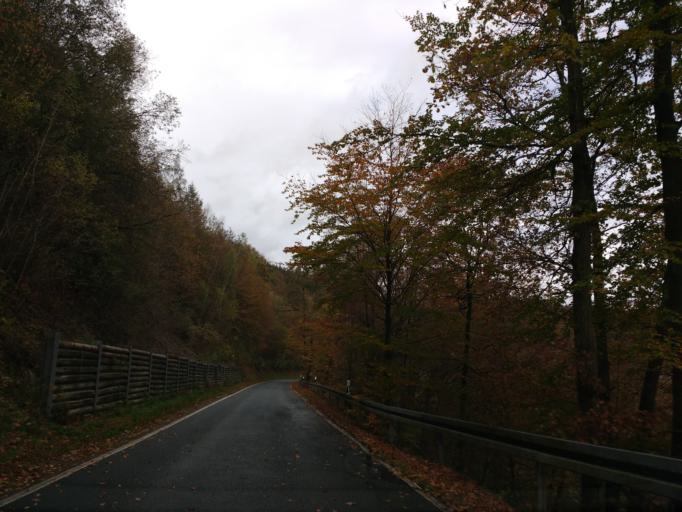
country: DE
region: Hesse
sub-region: Regierungsbezirk Kassel
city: Vohl
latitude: 51.1811
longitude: 8.9447
